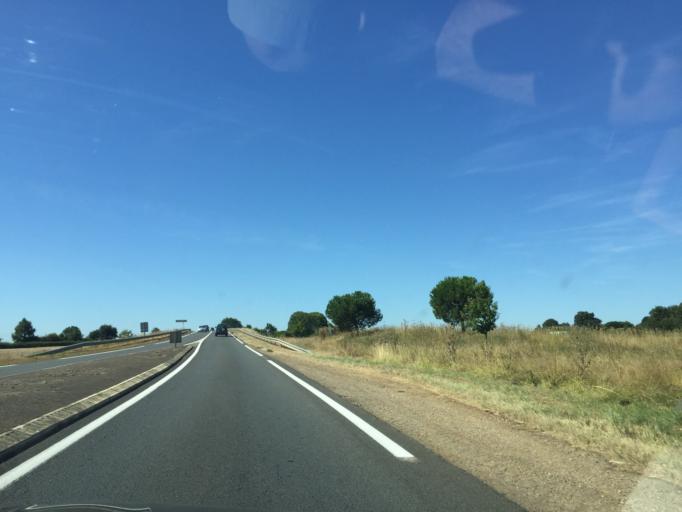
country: FR
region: Poitou-Charentes
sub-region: Departement de la Vienne
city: Lusignan
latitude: 46.4596
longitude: 0.1494
